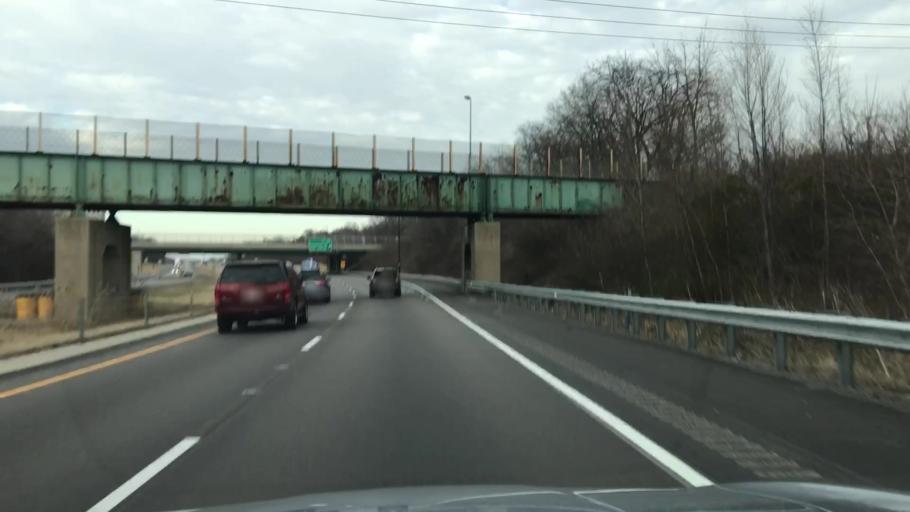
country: US
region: Illinois
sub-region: Sangamon County
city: Southern View
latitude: 39.7567
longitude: -89.6062
